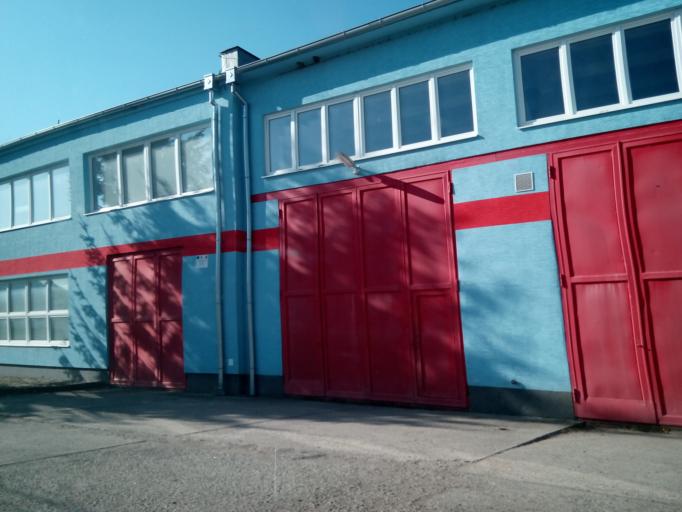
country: SK
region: Kosicky
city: Dobsina
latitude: 48.7155
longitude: 20.2758
